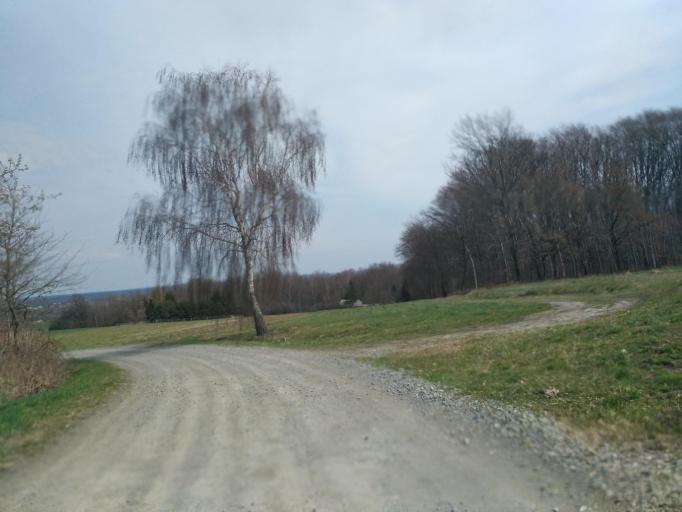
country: PL
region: Subcarpathian Voivodeship
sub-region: Powiat ropczycko-sedziszowski
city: Iwierzyce
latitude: 50.0400
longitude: 21.7219
